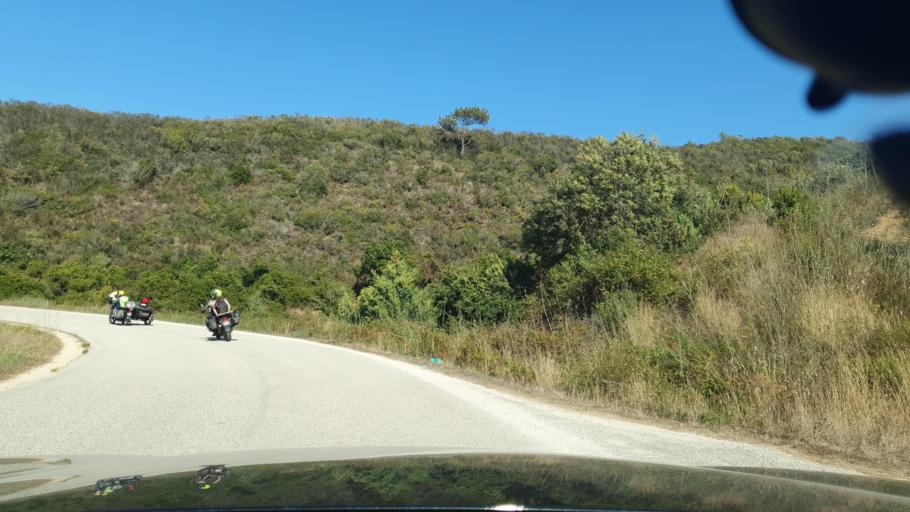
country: PT
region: Beja
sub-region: Odemira
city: Sao Teotonio
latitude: 37.4335
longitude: -8.7872
